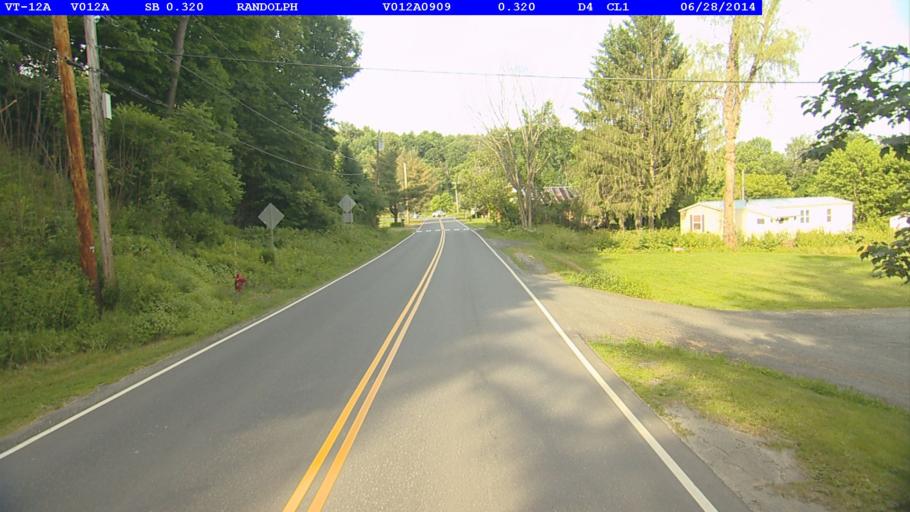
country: US
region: Vermont
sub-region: Orange County
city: Randolph
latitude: 43.9280
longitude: -72.6714
